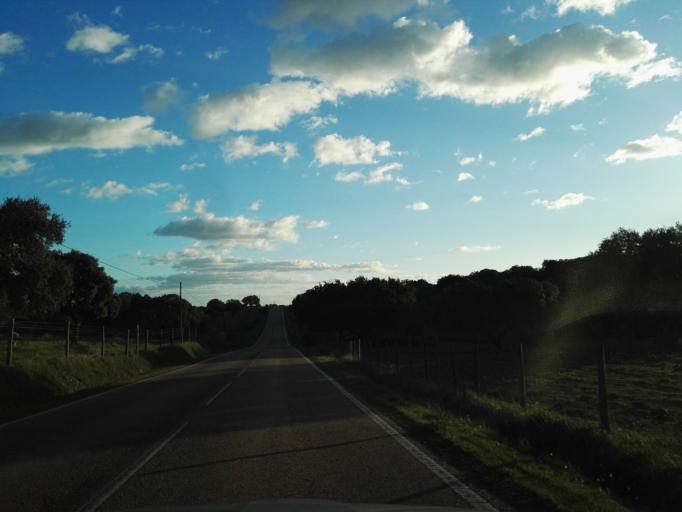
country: PT
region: Portalegre
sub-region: Elvas
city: Elvas
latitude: 38.8168
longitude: -7.1667
